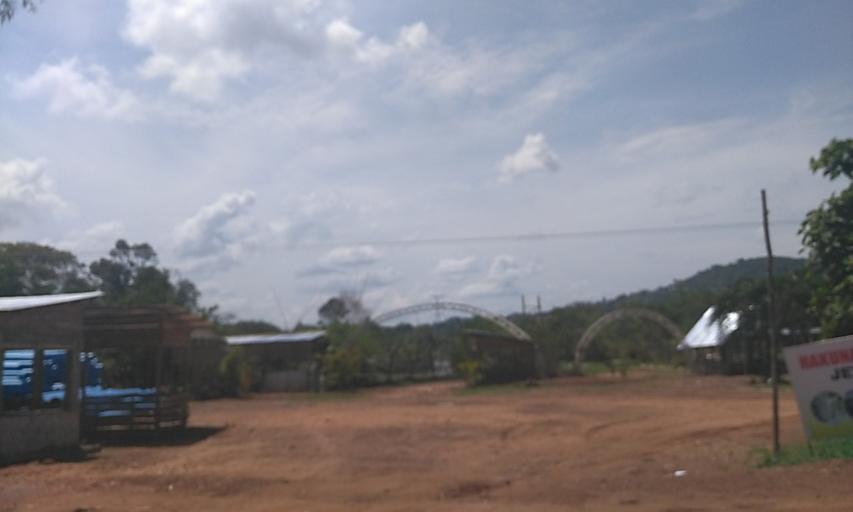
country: UG
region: Central Region
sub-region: Wakiso District
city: Wakiso
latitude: 0.3931
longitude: 32.5024
